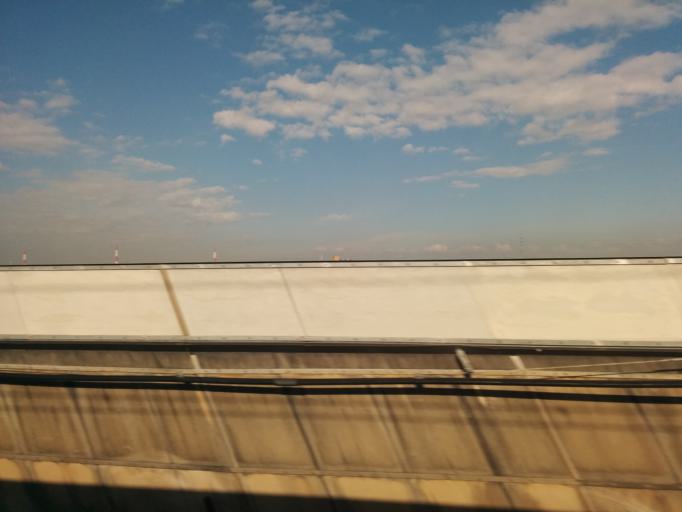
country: JP
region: Aichi
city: Chiryu
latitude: 35.0034
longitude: 137.0182
